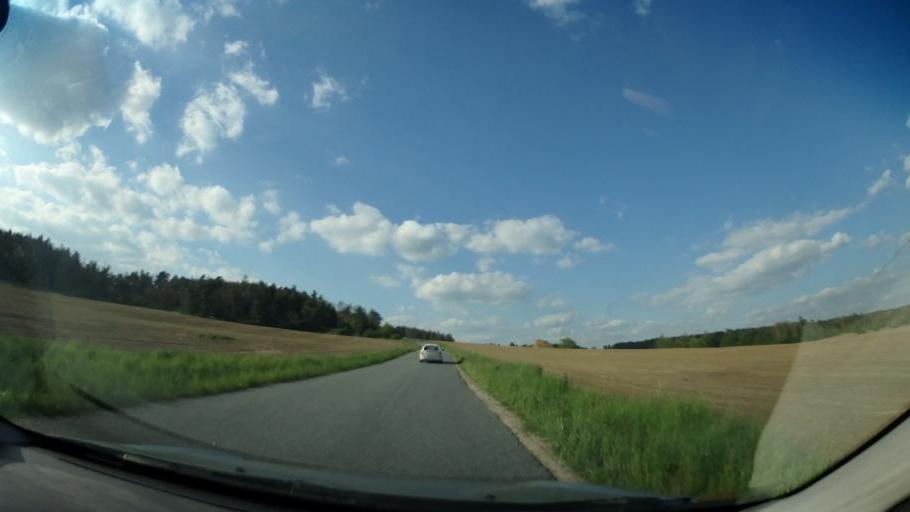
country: CZ
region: Vysocina
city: Budisov
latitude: 49.3012
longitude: 15.9803
